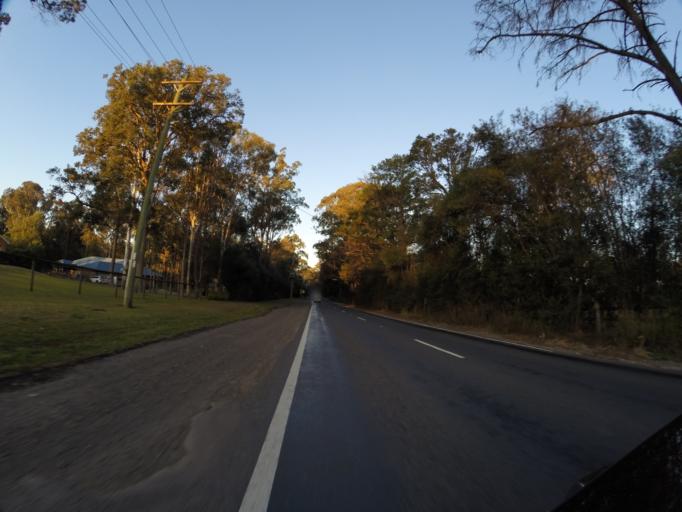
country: AU
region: New South Wales
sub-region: Camden
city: Cobbitty
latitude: -34.0159
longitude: 150.6930
